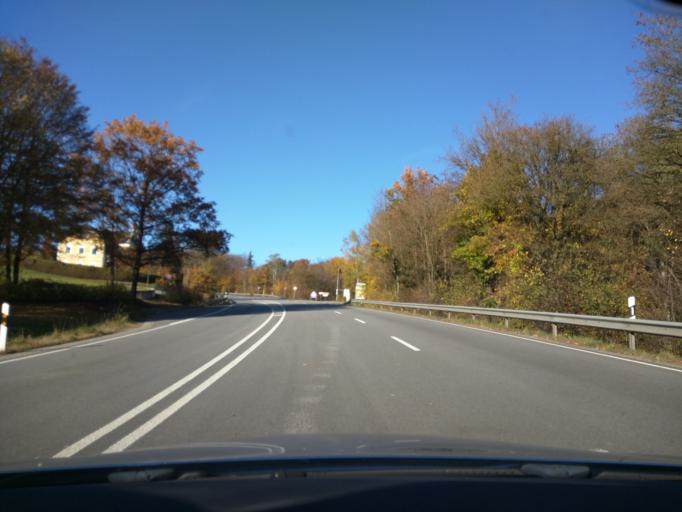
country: DE
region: Bavaria
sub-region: Lower Bavaria
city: Salzweg
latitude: 48.5915
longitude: 13.4781
